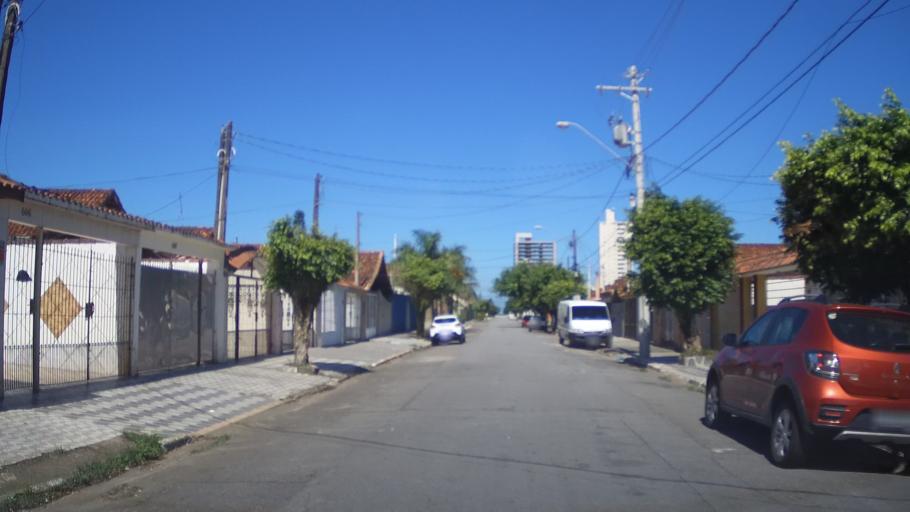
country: BR
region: Sao Paulo
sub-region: Praia Grande
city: Praia Grande
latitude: -24.0363
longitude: -46.5049
